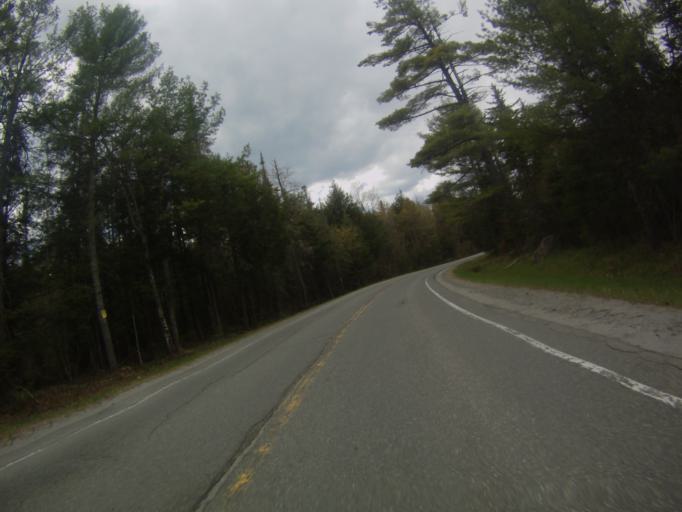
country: US
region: New York
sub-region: Essex County
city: Mineville
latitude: 44.0975
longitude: -73.5634
